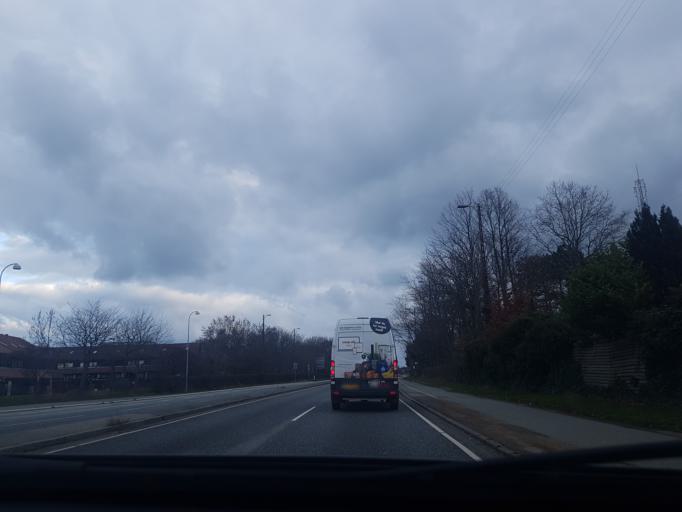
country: DK
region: Capital Region
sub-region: Ishoj Kommune
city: Ishoj
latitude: 55.6129
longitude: 12.3667
